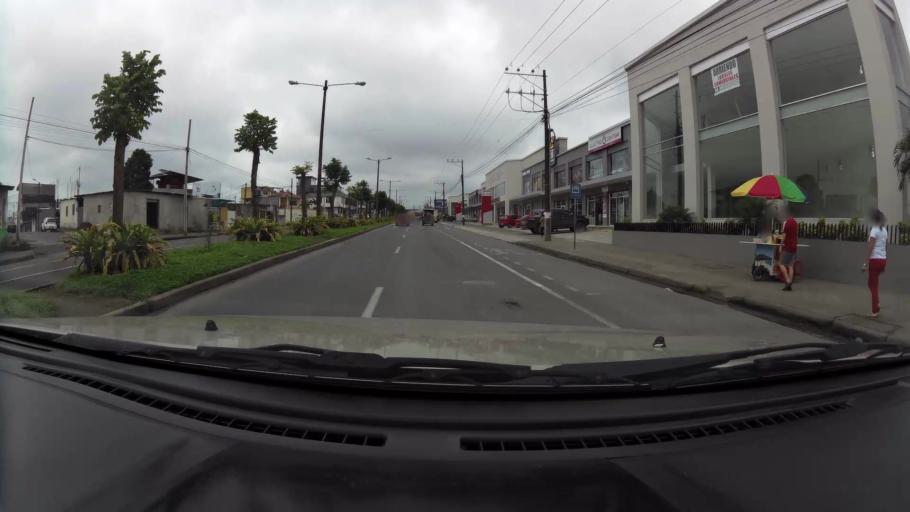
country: EC
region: Santo Domingo de los Tsachilas
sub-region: Canton Santo Domingo de los Colorados
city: Santo Domingo de los Colorados
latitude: -0.2654
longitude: -79.1718
